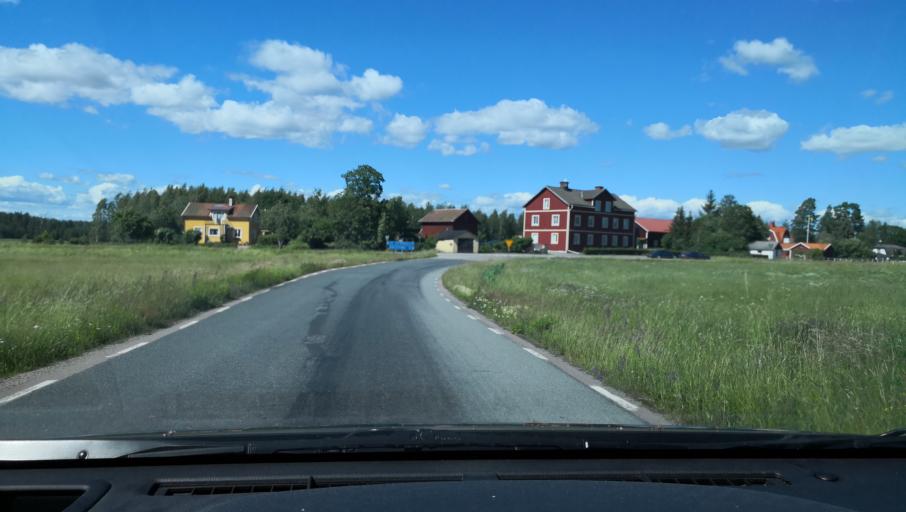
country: SE
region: Soedermanland
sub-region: Eskilstuna Kommun
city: Hallbybrunn
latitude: 59.3187
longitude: 16.3767
